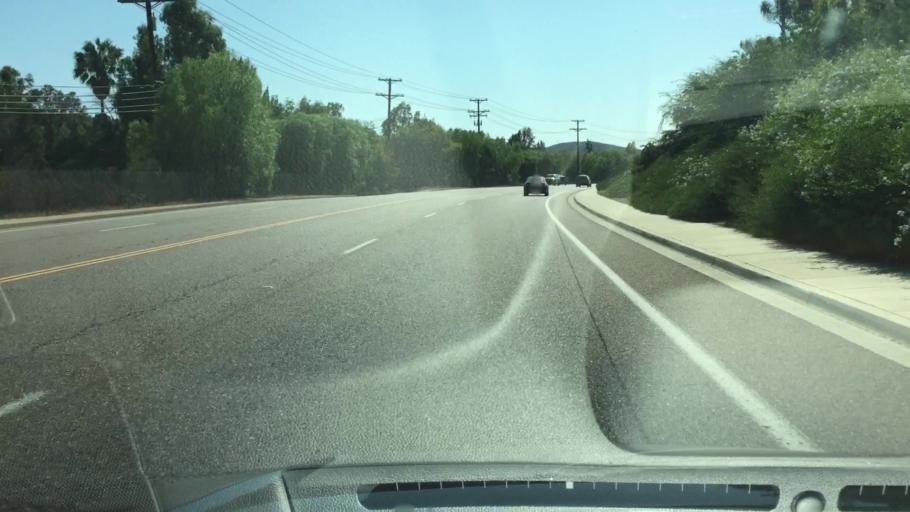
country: US
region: California
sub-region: San Diego County
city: Rancho San Diego
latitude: 32.7433
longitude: -116.9213
